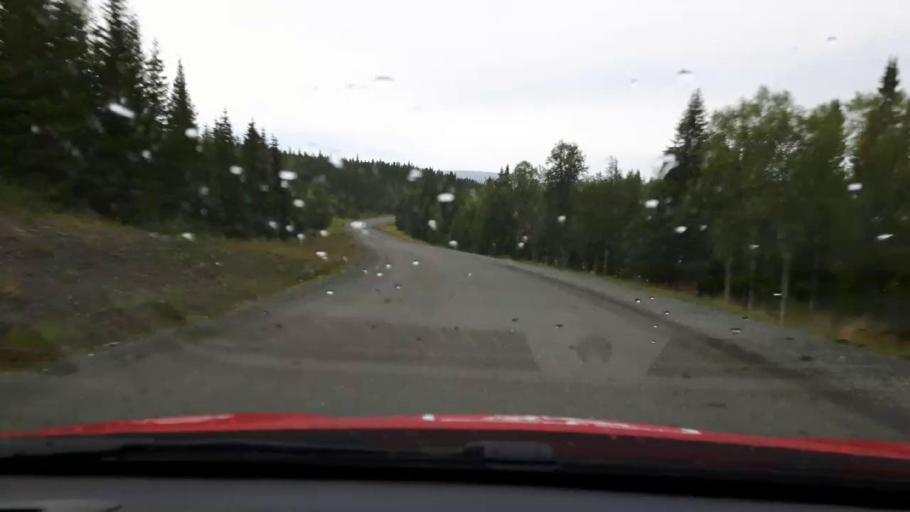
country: SE
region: Jaemtland
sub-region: Are Kommun
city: Are
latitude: 63.4157
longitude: 12.7594
